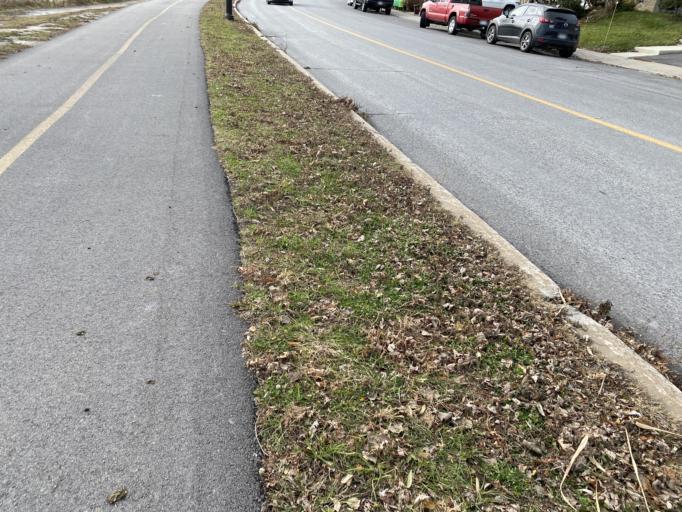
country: CA
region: Quebec
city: Saint-Raymond
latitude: 45.4167
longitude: -73.6102
